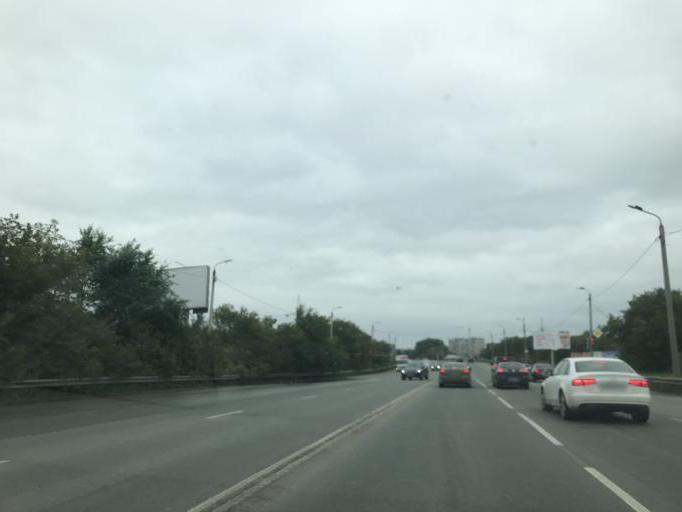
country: RU
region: Chelyabinsk
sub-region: Gorod Chelyabinsk
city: Chelyabinsk
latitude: 55.1652
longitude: 61.4282
